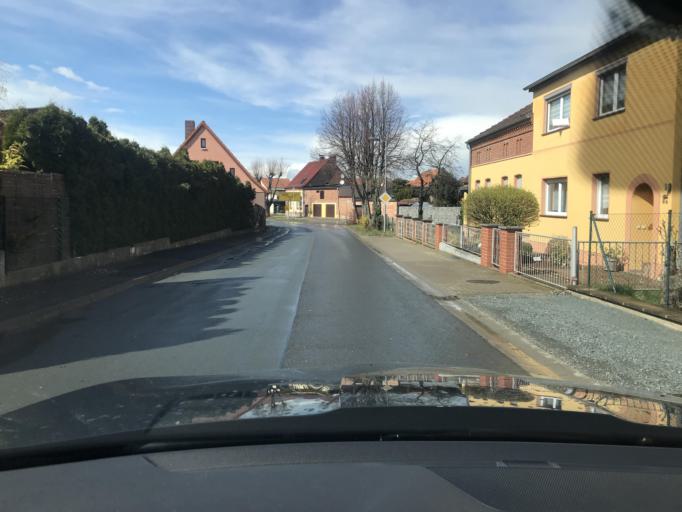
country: DE
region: Saxony-Anhalt
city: Hoym
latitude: 51.7313
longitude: 11.3530
